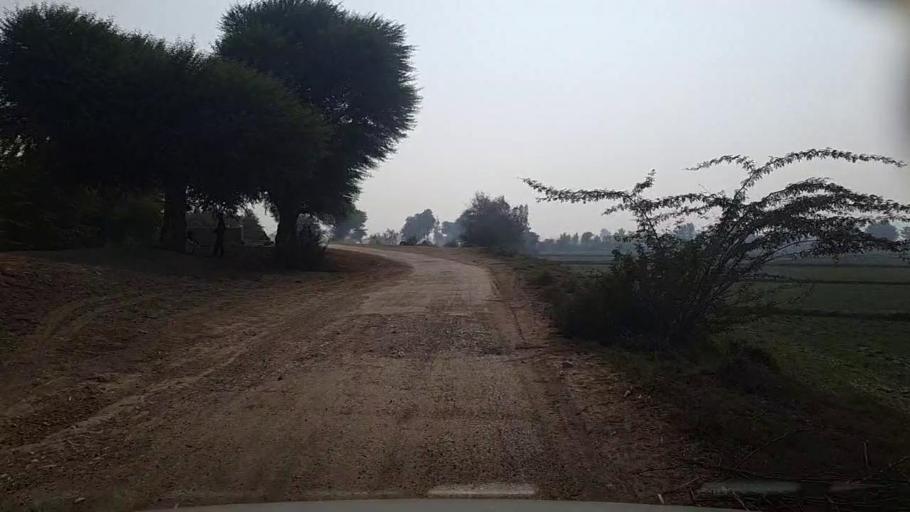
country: PK
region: Sindh
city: Setharja Old
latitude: 27.1315
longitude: 68.5119
